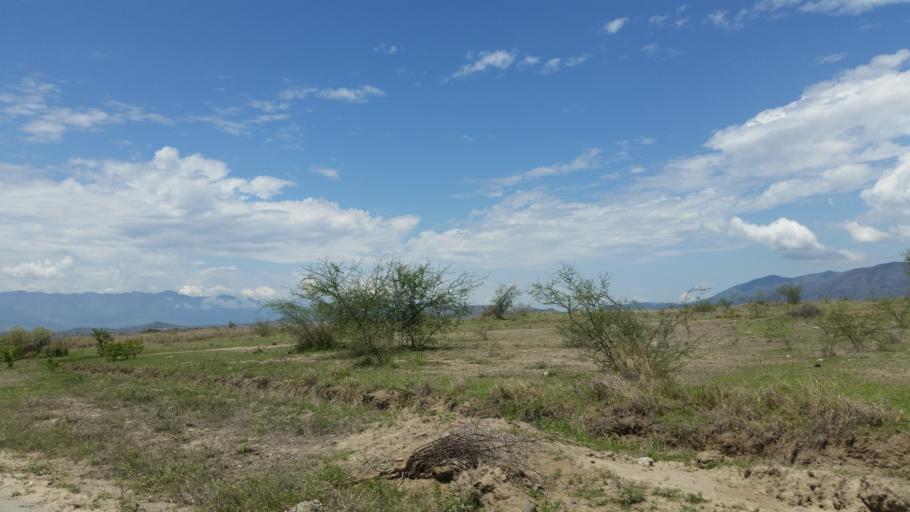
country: CO
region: Huila
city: Baraya
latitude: 3.2361
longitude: -75.1038
